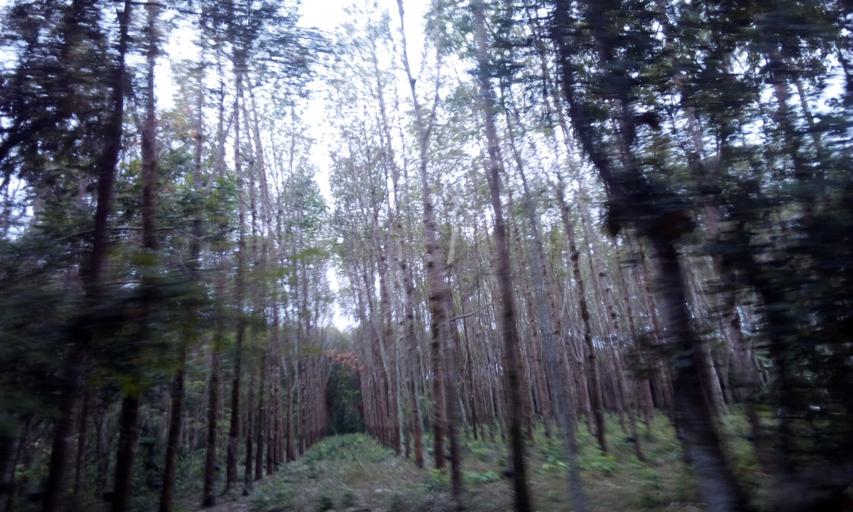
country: TH
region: Trat
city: Laem Ngop
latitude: 12.2099
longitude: 102.2943
